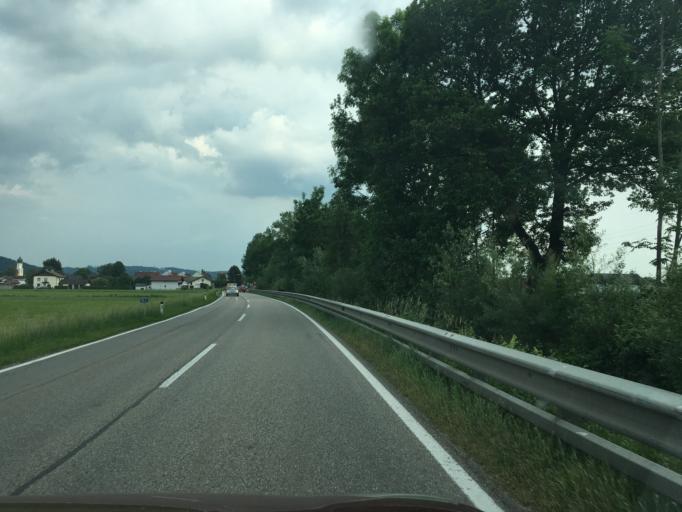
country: AT
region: Upper Austria
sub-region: Politischer Bezirk Braunau am Inn
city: Altheim
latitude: 48.1238
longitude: 13.1496
